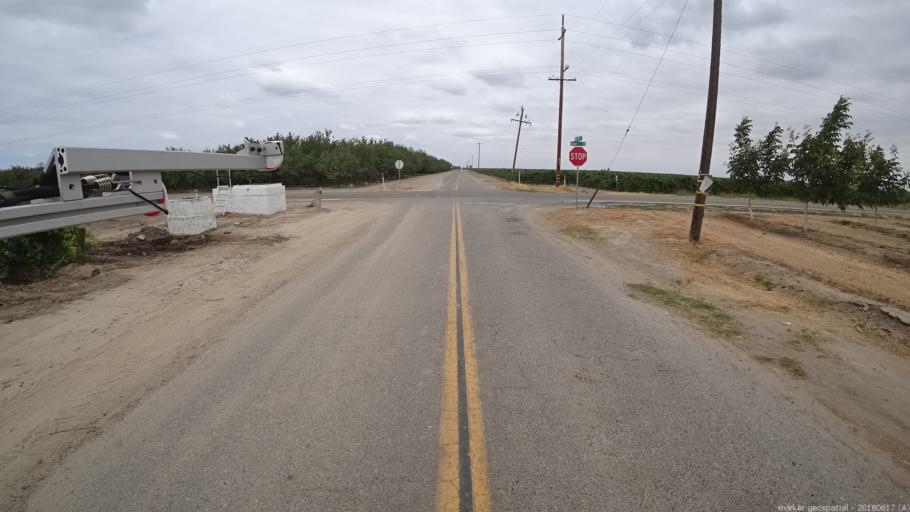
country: US
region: California
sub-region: Madera County
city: Madera
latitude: 36.9234
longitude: -120.1560
